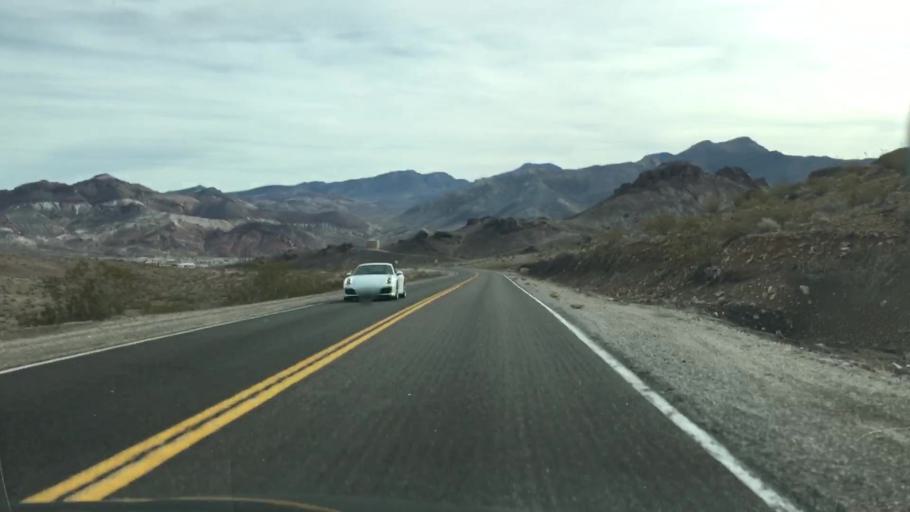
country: US
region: Nevada
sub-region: Nye County
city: Beatty
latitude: 36.9027
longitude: -116.7818
